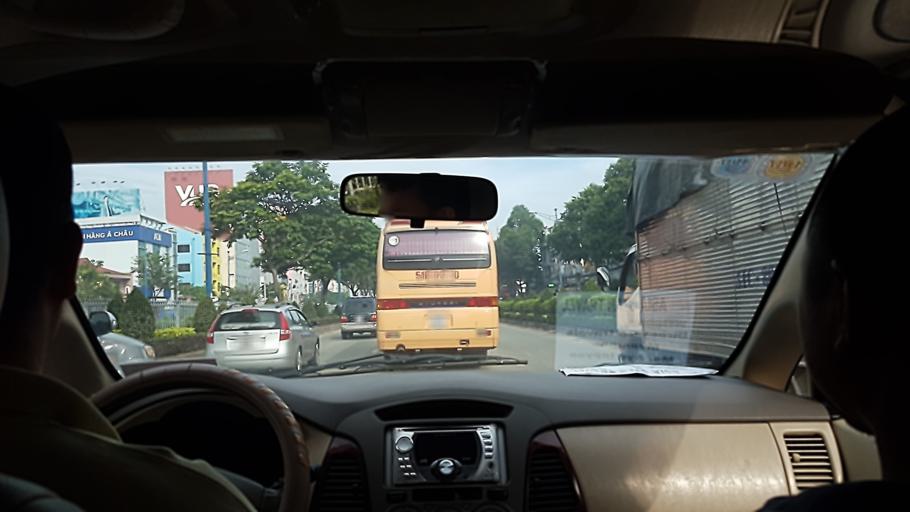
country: VN
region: Ho Chi Minh City
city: Ho Chi Minh City
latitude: 10.8320
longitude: 106.6222
